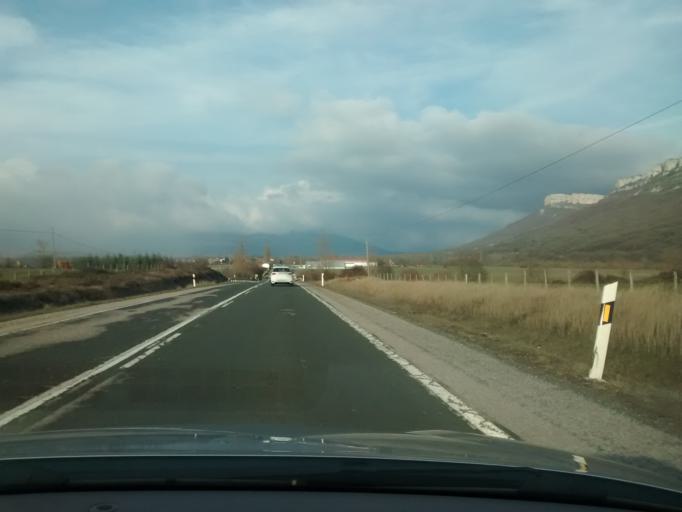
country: ES
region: Castille and Leon
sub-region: Provincia de Burgos
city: Espinosa de los Monteros
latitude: 43.0521
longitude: -3.4833
